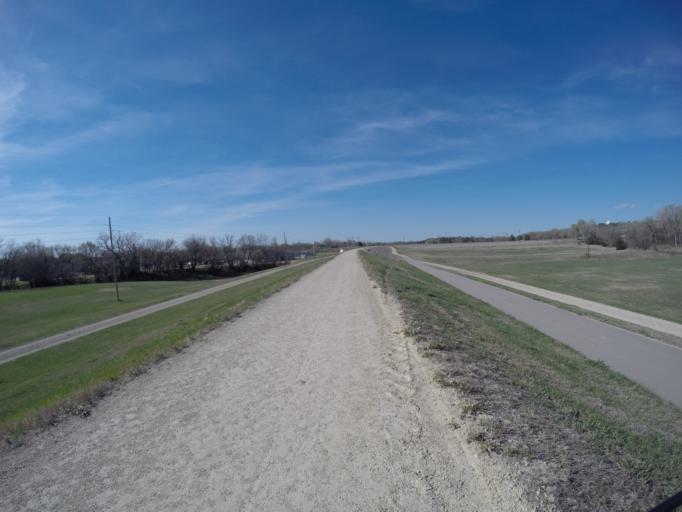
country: US
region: Kansas
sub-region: Saline County
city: Salina
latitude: 38.8245
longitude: -97.5877
